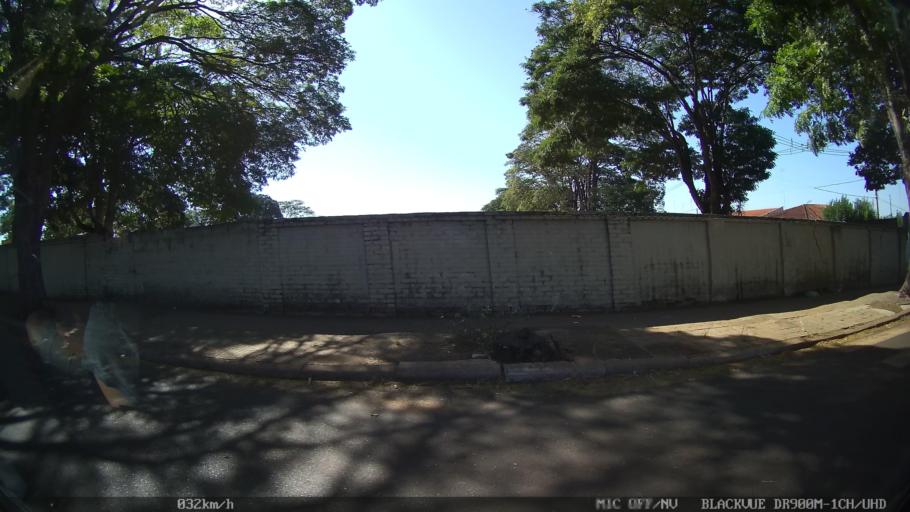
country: BR
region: Sao Paulo
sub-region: Batatais
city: Batatais
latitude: -20.9030
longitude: -47.5817
